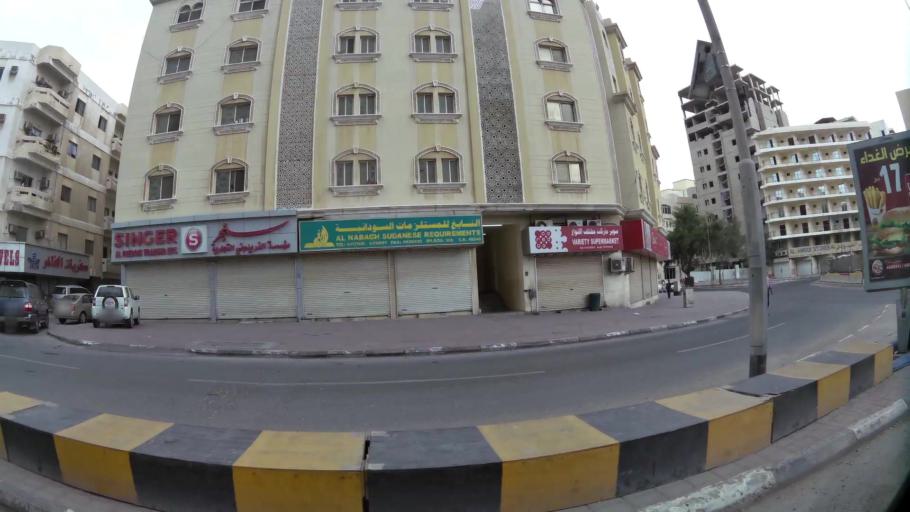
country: QA
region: Baladiyat ad Dawhah
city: Doha
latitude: 25.2867
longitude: 51.5404
